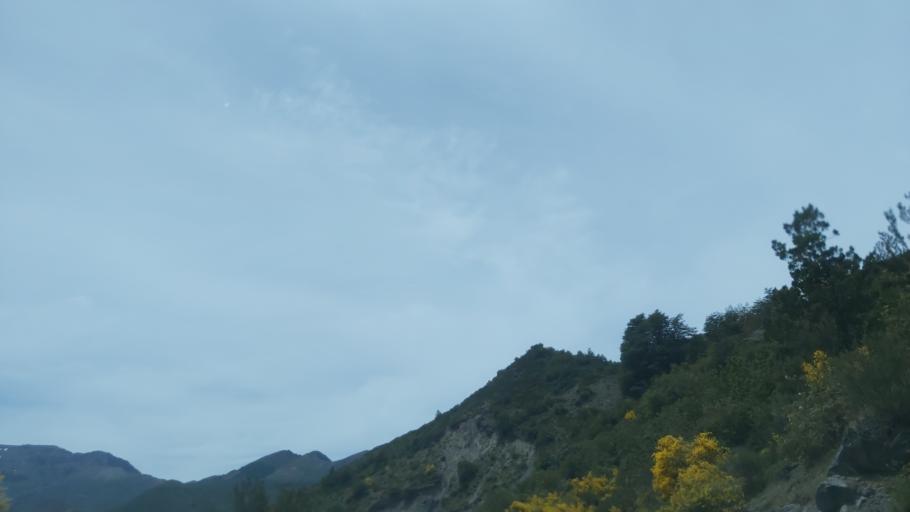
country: AR
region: Neuquen
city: Andacollo
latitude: -37.3914
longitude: -71.4023
